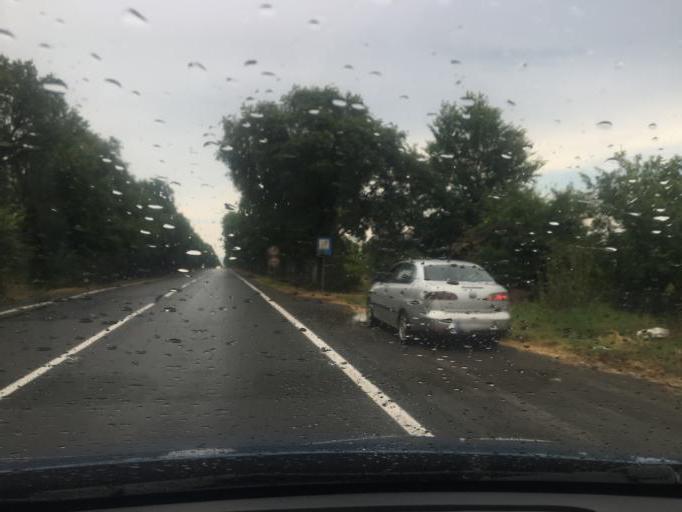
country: BG
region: Burgas
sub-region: Obshtina Pomorie
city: Pomorie
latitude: 42.5807
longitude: 27.6060
